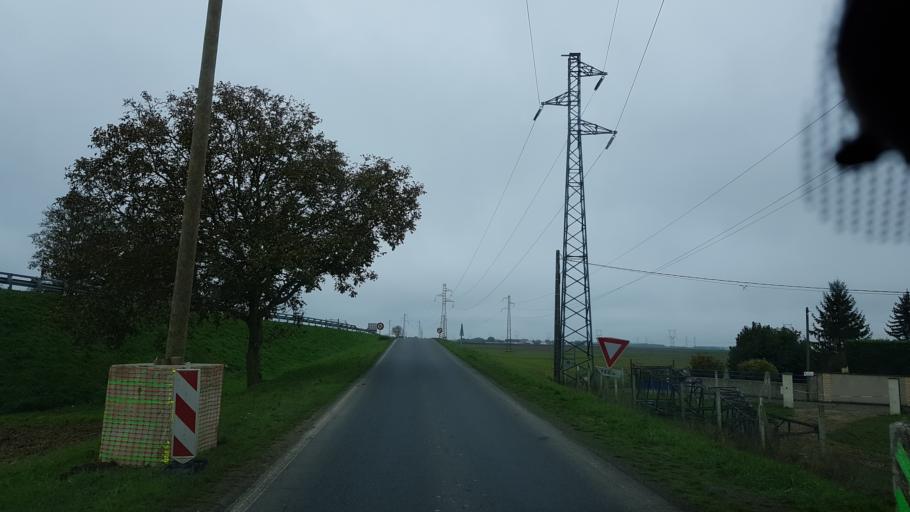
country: FR
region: Ile-de-France
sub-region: Departement de l'Essonne
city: Angerville
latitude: 48.3172
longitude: 1.9955
